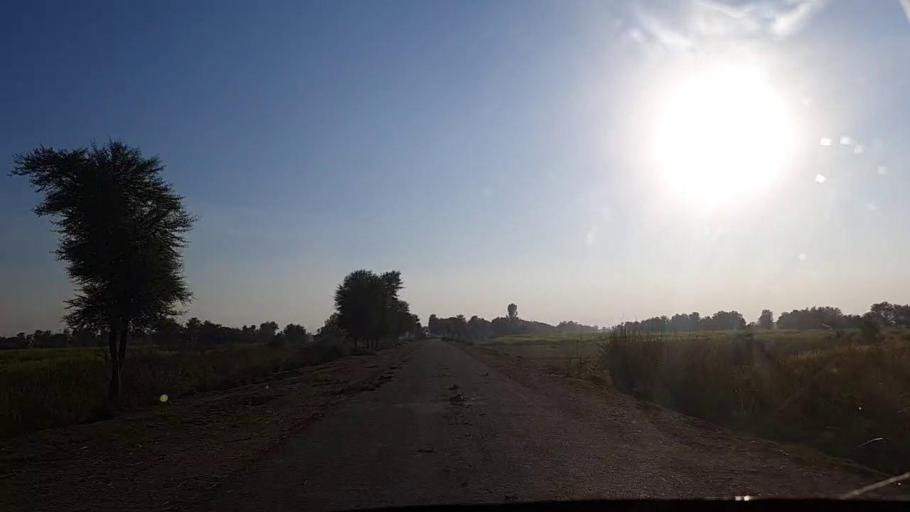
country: PK
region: Sindh
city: Sobhadero
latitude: 27.4204
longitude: 68.4050
